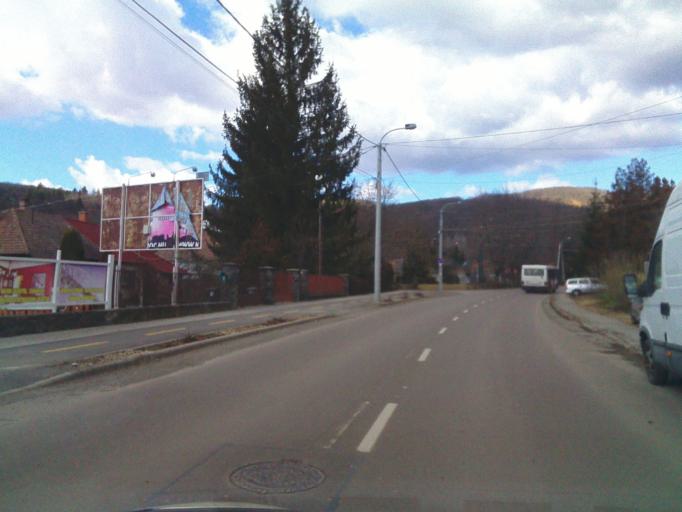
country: HU
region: Nograd
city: Salgotarjan
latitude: 48.1217
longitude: 19.8049
